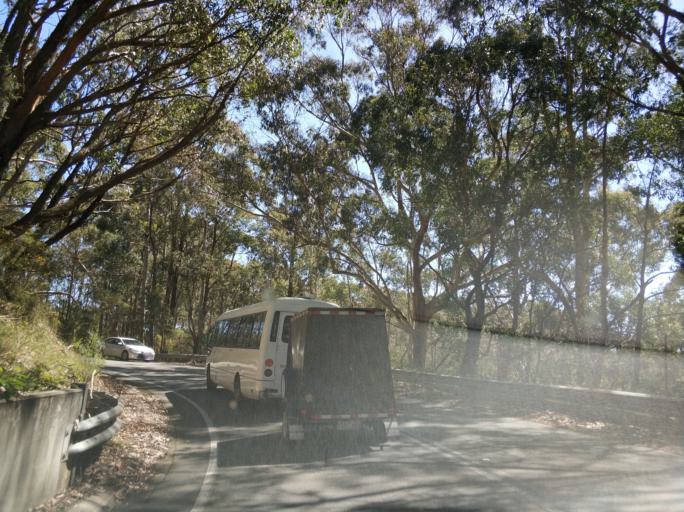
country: AU
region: Victoria
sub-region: Colac-Otway
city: Apollo Bay
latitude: -38.7461
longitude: 143.2707
